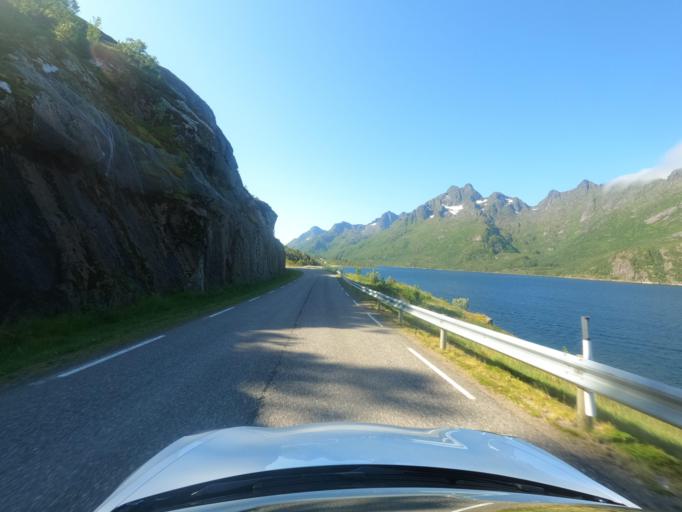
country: NO
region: Nordland
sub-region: Hadsel
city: Stokmarknes
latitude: 68.4399
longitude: 15.1877
